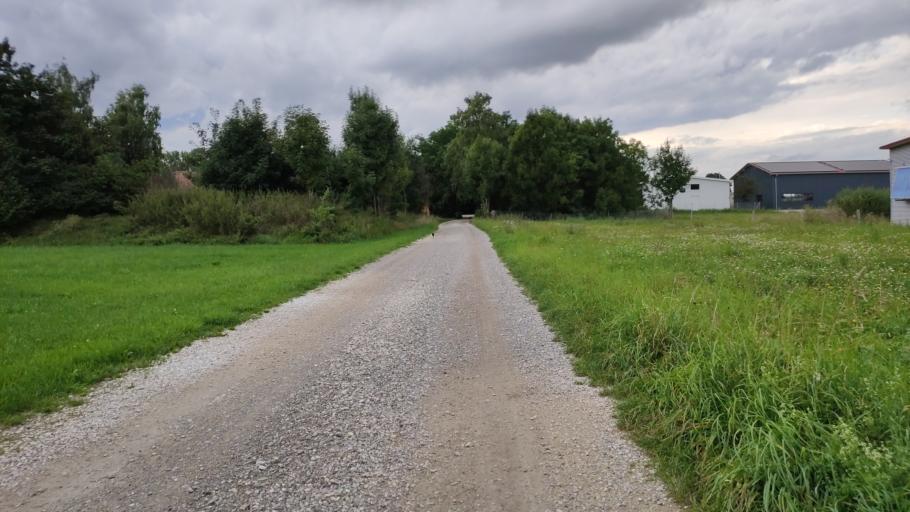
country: DE
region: Bavaria
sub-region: Swabia
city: Oberottmarshausen
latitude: 48.2401
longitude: 10.8608
